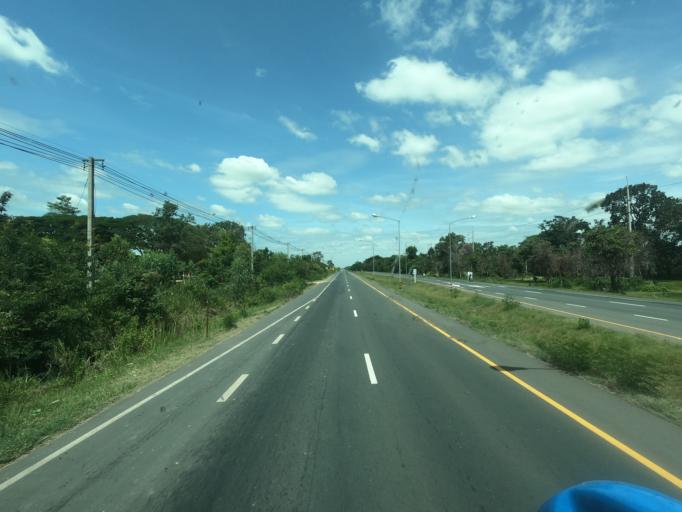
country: TH
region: Surin
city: Prasat
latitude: 14.6241
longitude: 103.3838
